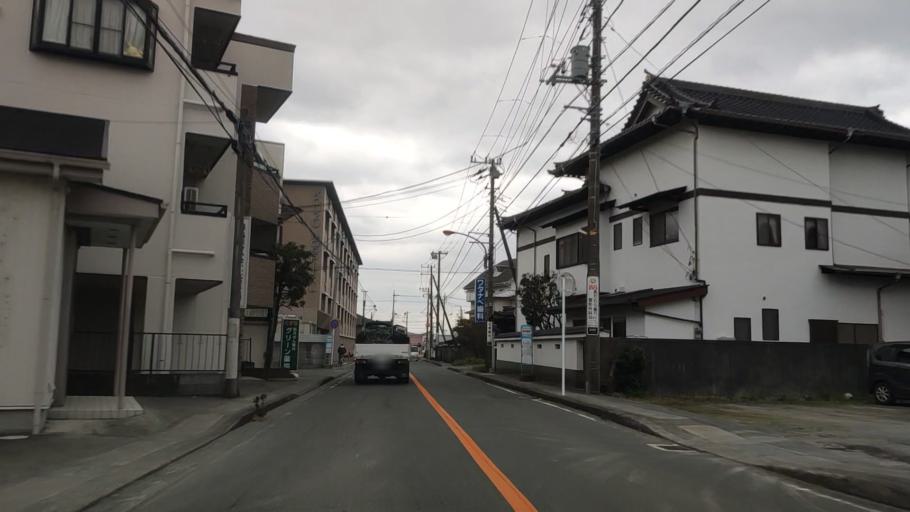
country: JP
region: Kanagawa
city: Odawara
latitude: 35.2834
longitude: 139.1972
